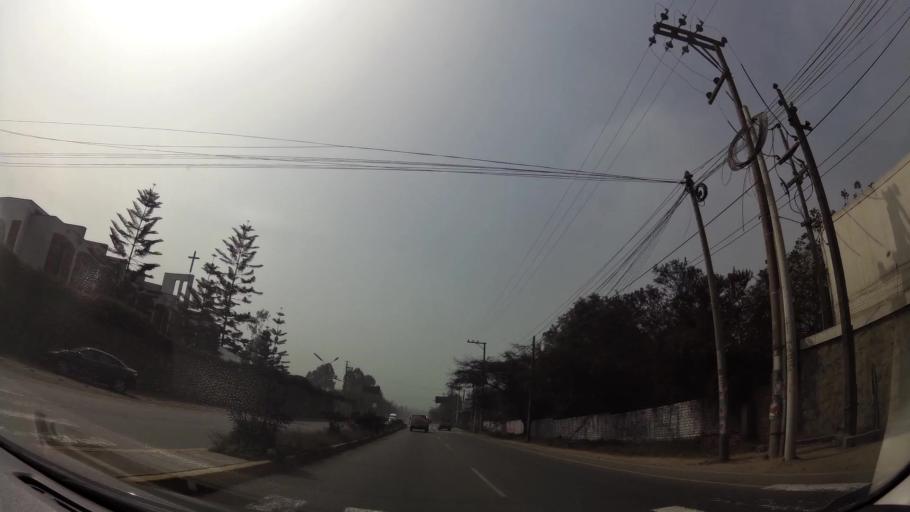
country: PE
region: Lima
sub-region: Lima
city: Chosica
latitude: -11.9581
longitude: -76.7342
